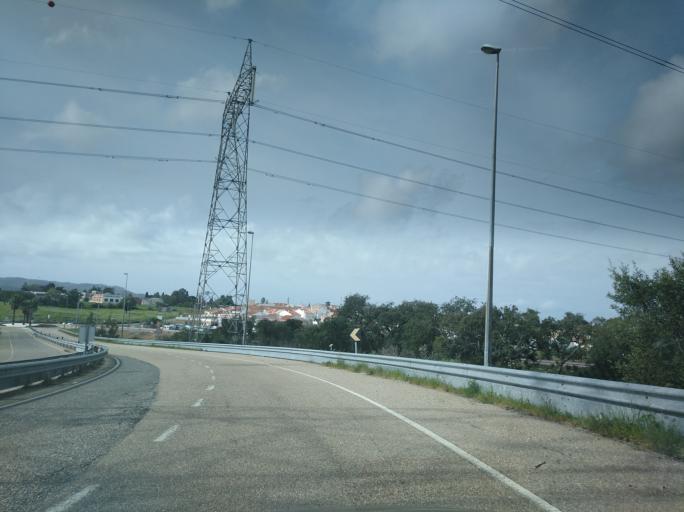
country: PT
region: Setubal
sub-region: Grandola
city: Grandola
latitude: 38.1692
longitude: -8.5525
